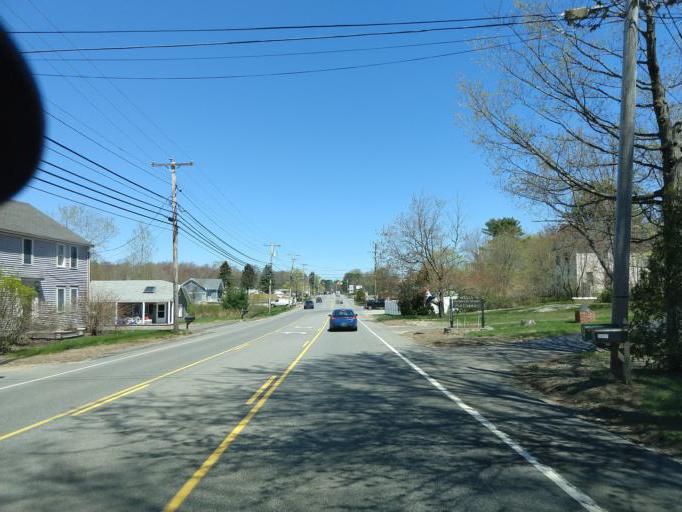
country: US
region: Maine
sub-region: York County
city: Wells Beach Station
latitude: 43.3349
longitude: -70.5691
